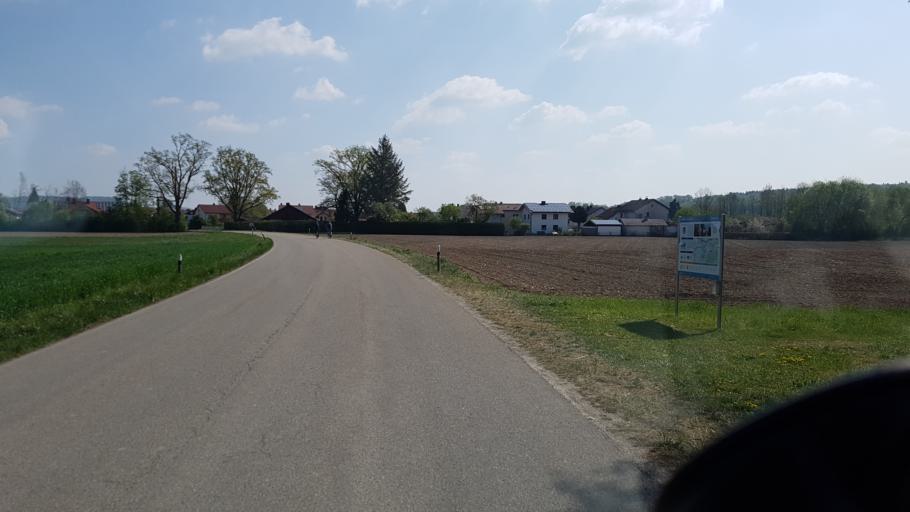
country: DE
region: Bavaria
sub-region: Upper Bavaria
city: Perach
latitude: 48.2421
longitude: 12.7432
